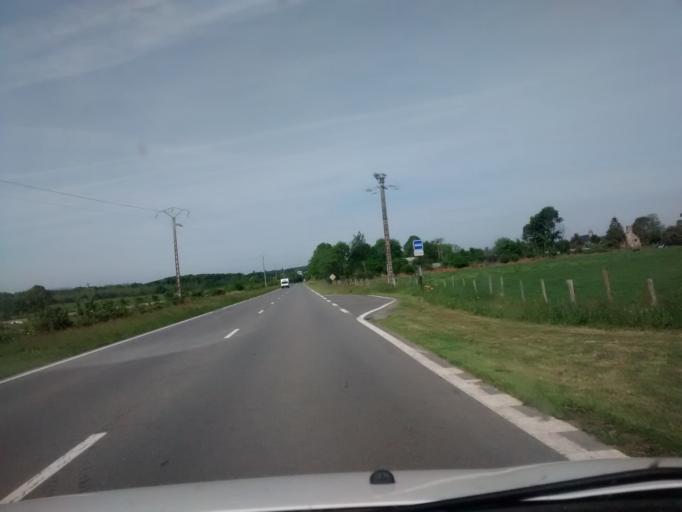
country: FR
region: Brittany
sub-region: Departement d'Ille-et-Vilaine
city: Tremblay
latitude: 48.4240
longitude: -1.4375
